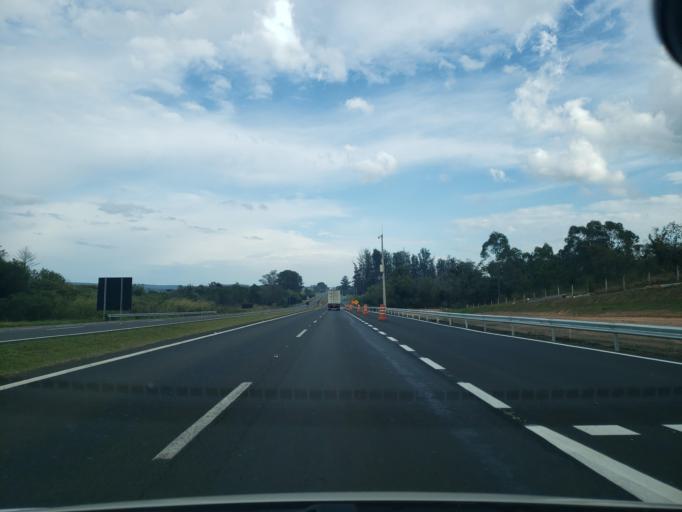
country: BR
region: Sao Paulo
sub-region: Itirapina
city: Itirapina
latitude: -22.2643
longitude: -47.9084
